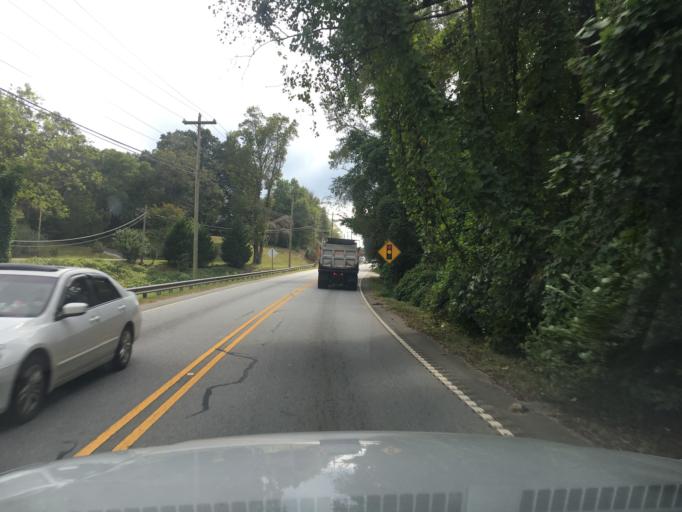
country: US
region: South Carolina
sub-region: Greenville County
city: Greer
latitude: 34.9584
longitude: -82.2306
